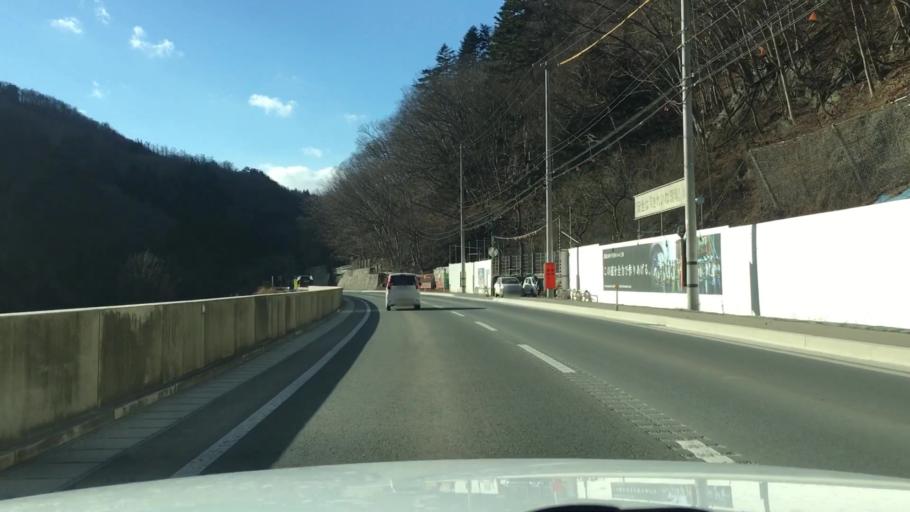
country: JP
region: Iwate
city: Miyako
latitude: 39.6014
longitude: 141.7098
